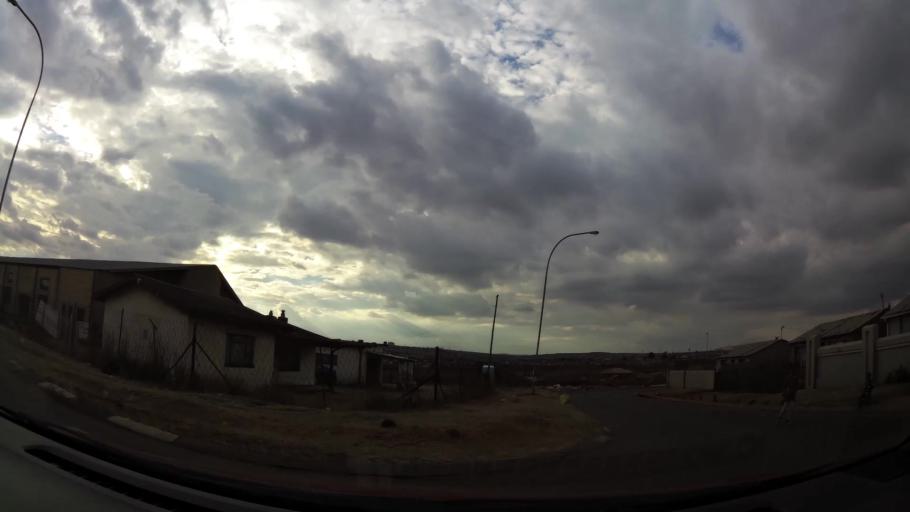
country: ZA
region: Gauteng
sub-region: City of Johannesburg Metropolitan Municipality
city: Soweto
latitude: -26.2416
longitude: 27.8156
